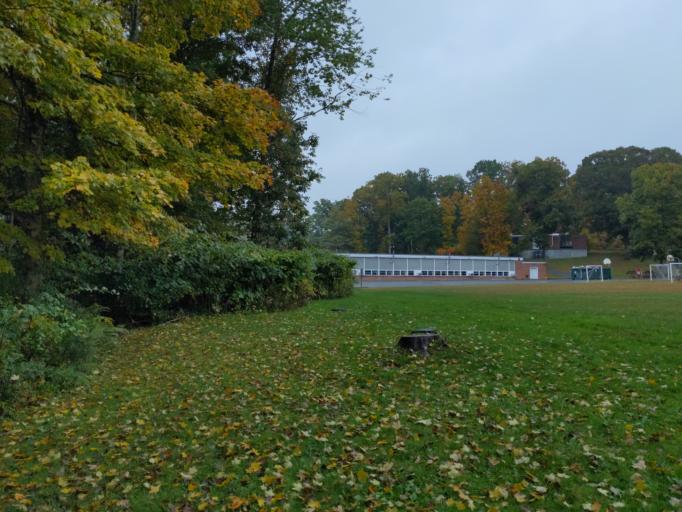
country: US
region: Connecticut
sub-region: New Haven County
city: Oxford
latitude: 41.4375
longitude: -73.1173
